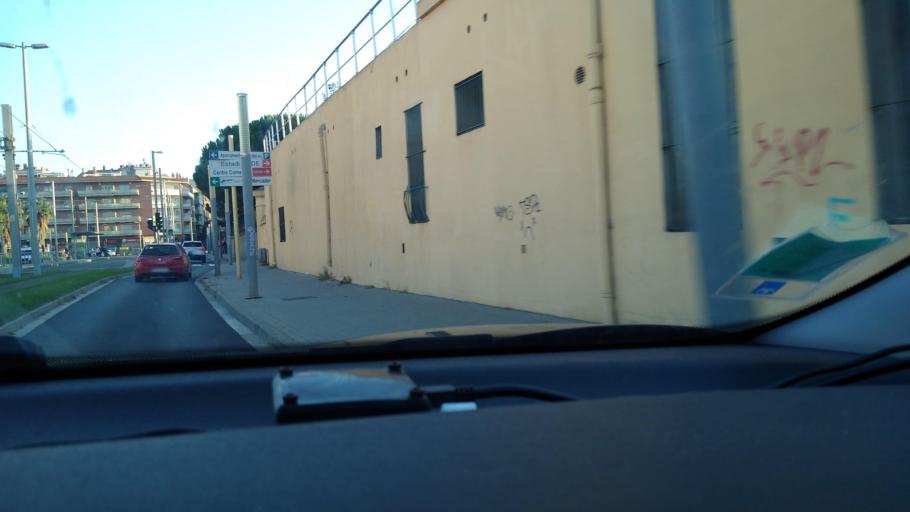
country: ES
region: Catalonia
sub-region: Provincia de Barcelona
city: Sant Joan Despi
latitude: 41.3573
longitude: 2.0654
